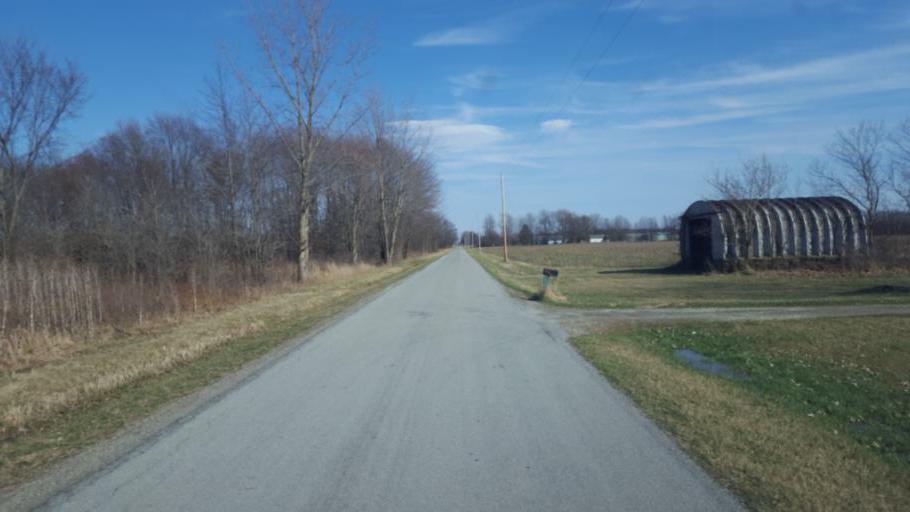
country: US
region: Ohio
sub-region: Wyandot County
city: Upper Sandusky
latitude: 40.6945
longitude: -83.3722
